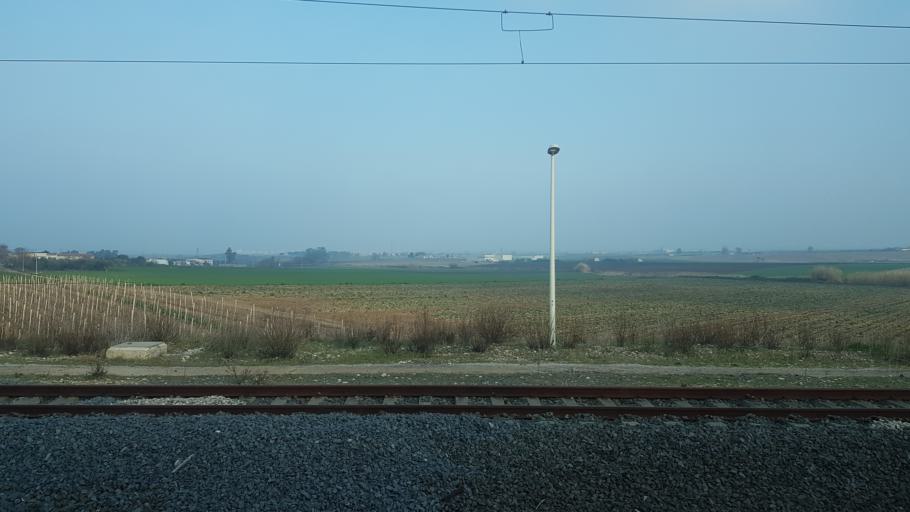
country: IT
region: Apulia
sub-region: Provincia di Foggia
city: Lesina
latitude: 41.8531
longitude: 15.2958
